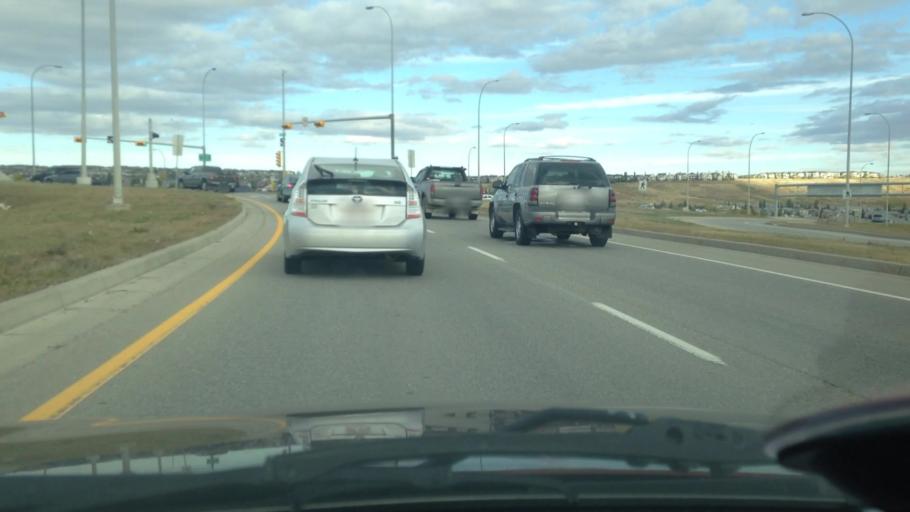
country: CA
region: Alberta
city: Calgary
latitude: 51.1559
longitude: -114.1160
